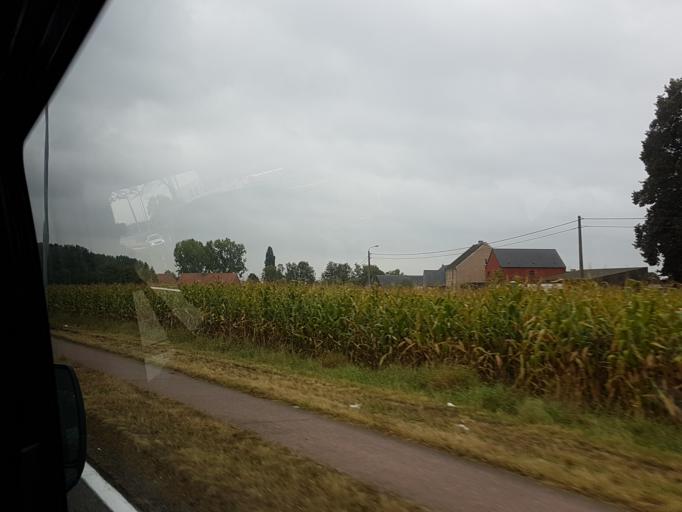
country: BE
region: Flanders
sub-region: Provincie Antwerpen
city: Geel
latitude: 51.1497
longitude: 4.9787
